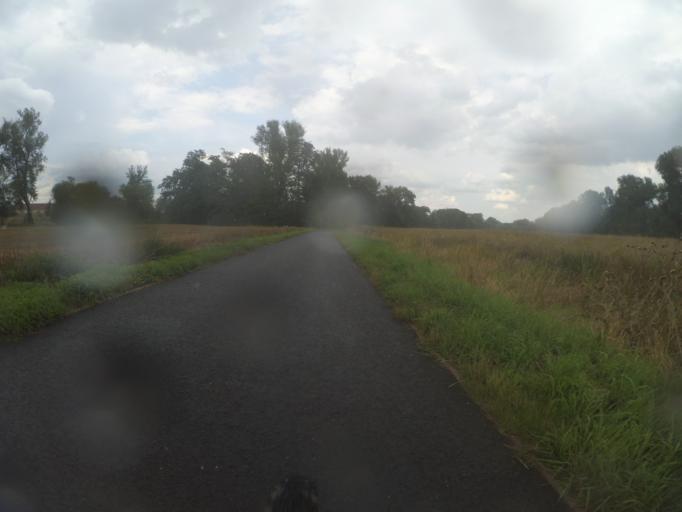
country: CZ
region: Central Bohemia
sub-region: Okres Melnik
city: Melnik
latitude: 50.3217
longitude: 14.4525
